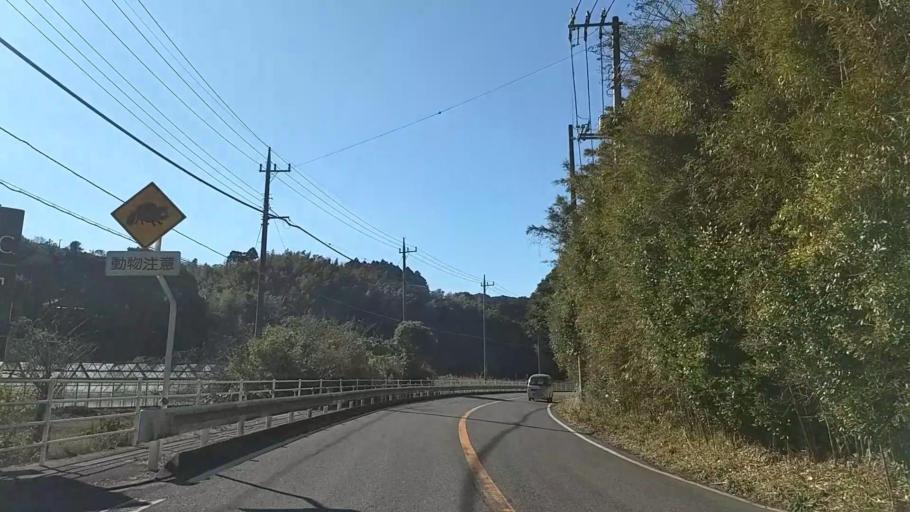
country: JP
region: Chiba
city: Tateyama
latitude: 34.9559
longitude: 139.8489
